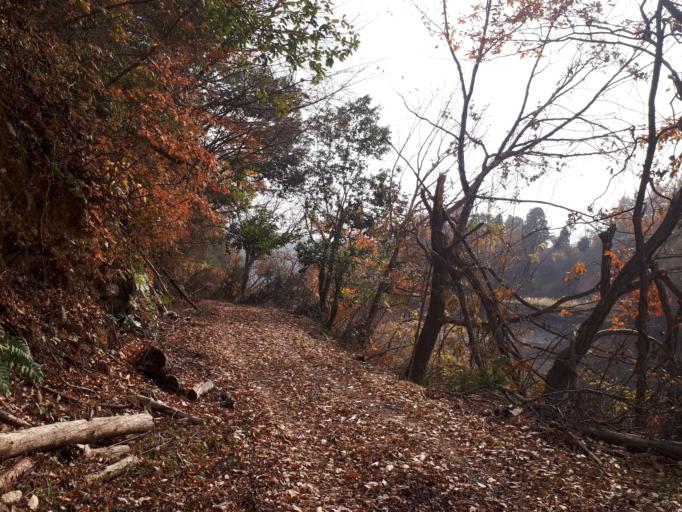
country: JP
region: Kyoto
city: Kameoka
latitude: 34.9628
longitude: 135.5243
